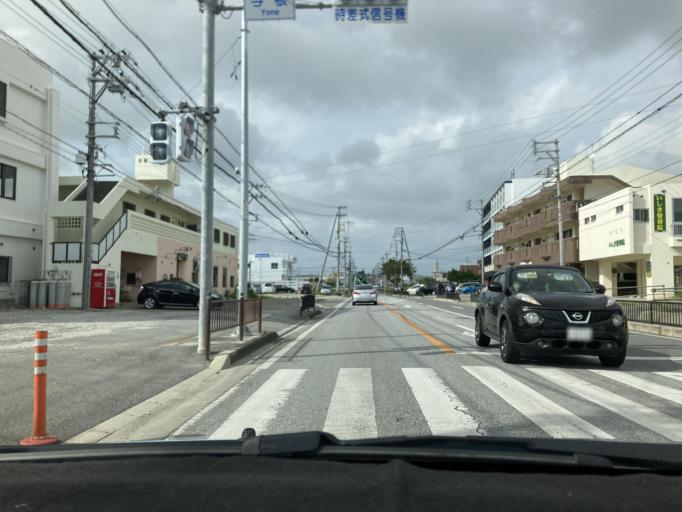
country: JP
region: Okinawa
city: Tomigusuku
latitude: 26.1648
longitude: 127.6686
